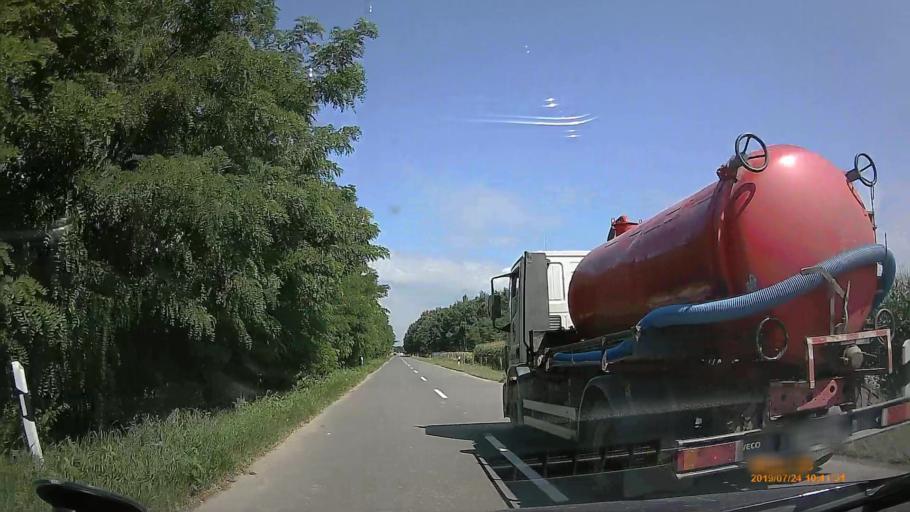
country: HU
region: Szabolcs-Szatmar-Bereg
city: Tarpa
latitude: 48.1925
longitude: 22.5477
